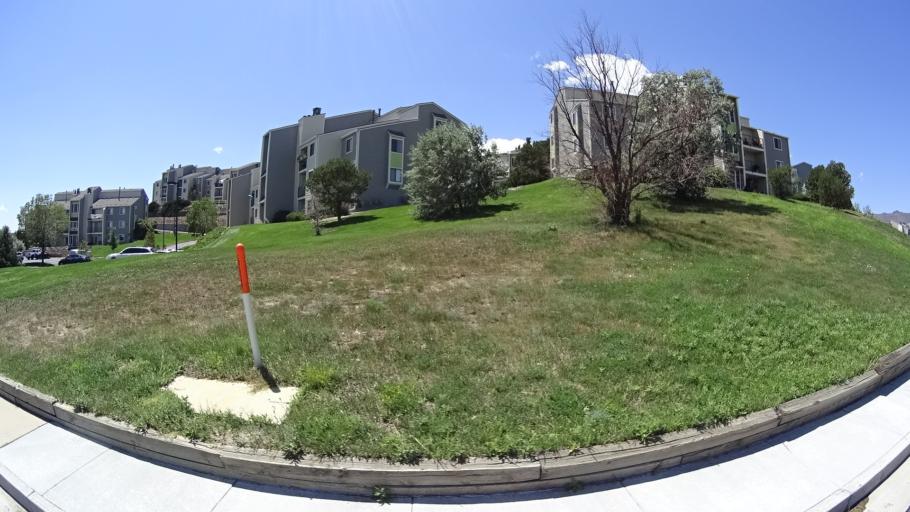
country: US
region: Colorado
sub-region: El Paso County
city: Air Force Academy
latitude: 38.9169
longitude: -104.8322
